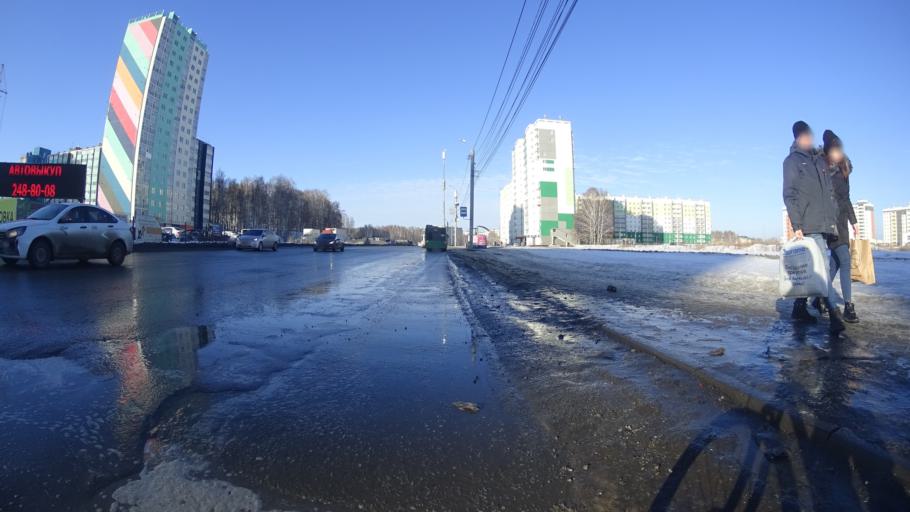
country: RU
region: Chelyabinsk
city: Roshchino
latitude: 55.2103
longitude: 61.2844
